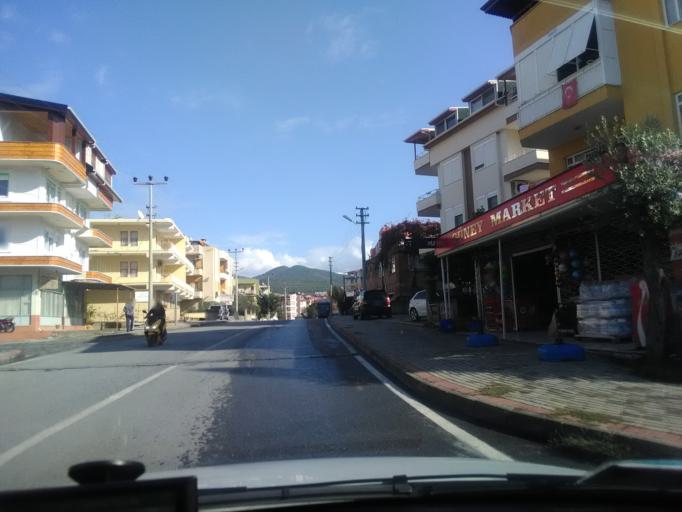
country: TR
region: Antalya
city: Gazipasa
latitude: 36.2745
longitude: 32.3120
